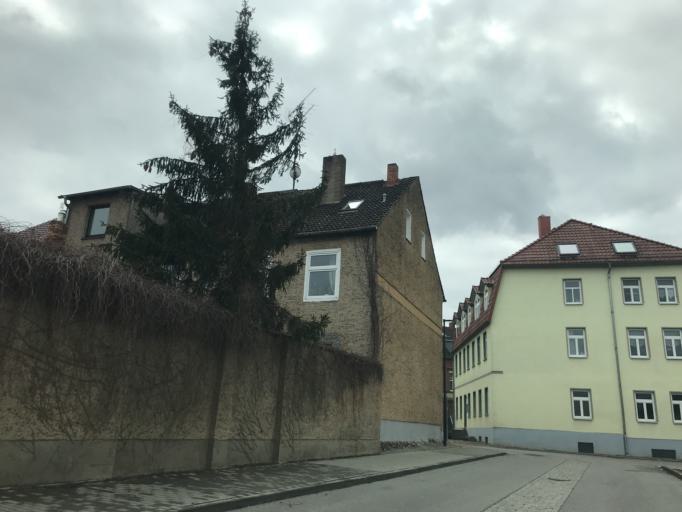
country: DE
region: Brandenburg
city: Luebben
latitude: 51.9425
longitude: 13.9015
